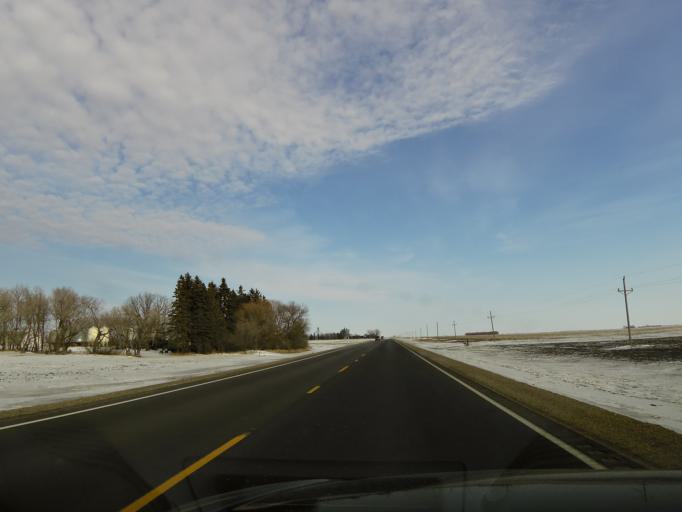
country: US
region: Minnesota
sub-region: Kittson County
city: Hallock
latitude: 48.5730
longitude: -97.1204
